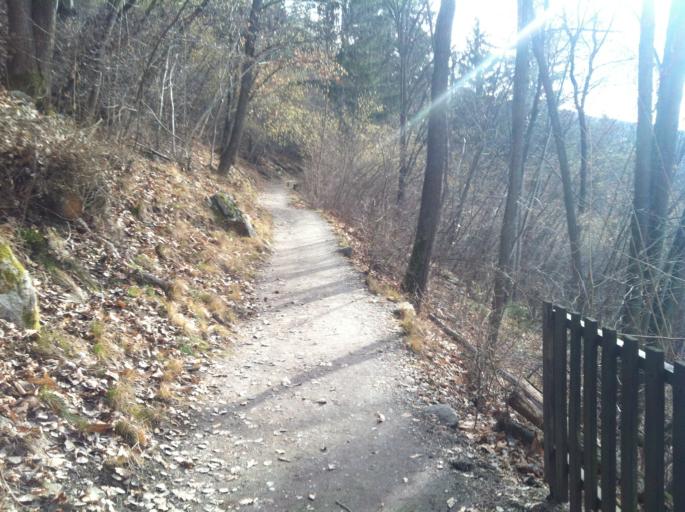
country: IT
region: Trentino-Alto Adige
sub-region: Bolzano
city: Bressanone
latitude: 46.7077
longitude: 11.6669
